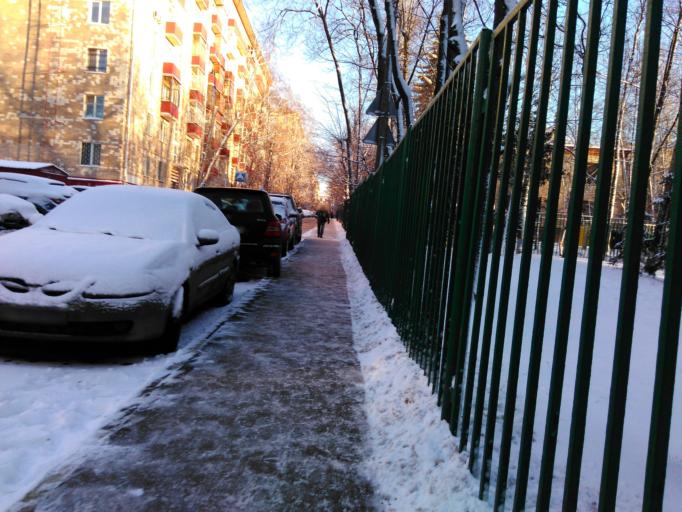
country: RU
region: Moskovskaya
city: Semenovskoye
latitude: 55.6874
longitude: 37.5294
